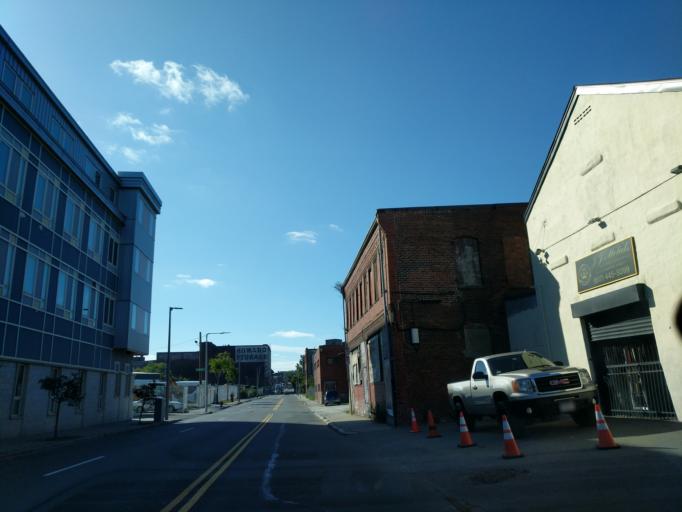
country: US
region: Massachusetts
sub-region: Suffolk County
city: South Boston
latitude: 42.3309
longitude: -71.0749
